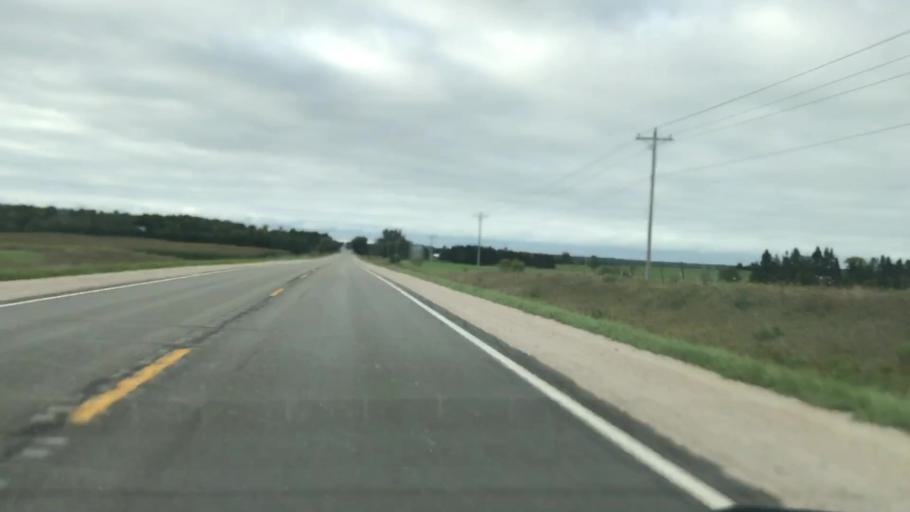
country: US
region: Michigan
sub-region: Luce County
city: Newberry
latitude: 46.1636
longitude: -85.5712
